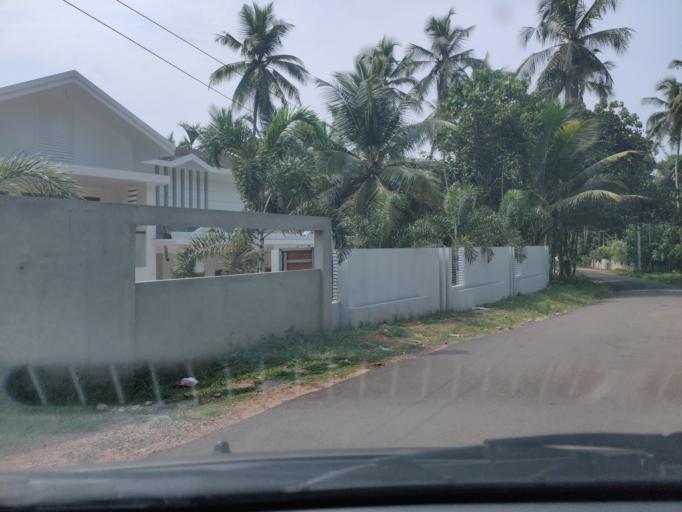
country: IN
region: Kerala
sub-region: Kozhikode
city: Kunnamangalam
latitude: 11.4196
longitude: 75.8731
